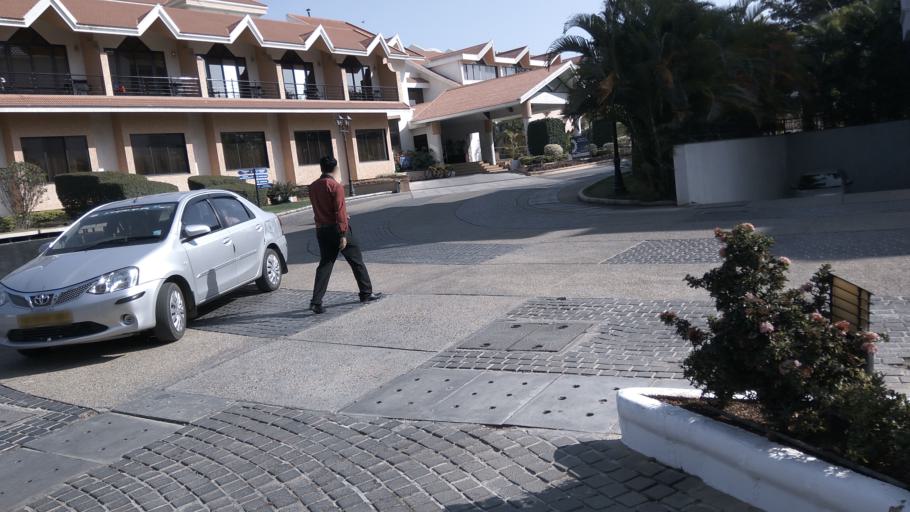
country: IN
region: Karnataka
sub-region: Bangalore Rural
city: Devanhalli
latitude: 13.2073
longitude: 77.6331
